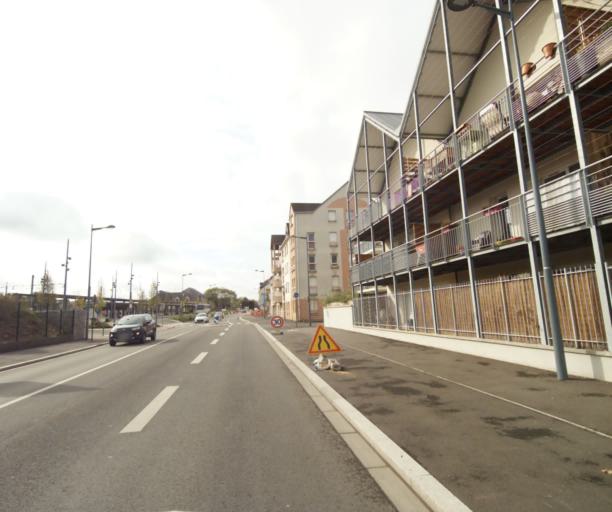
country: FR
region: Centre
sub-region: Departement d'Eure-et-Loir
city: Dreux
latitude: 48.7328
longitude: 1.3727
